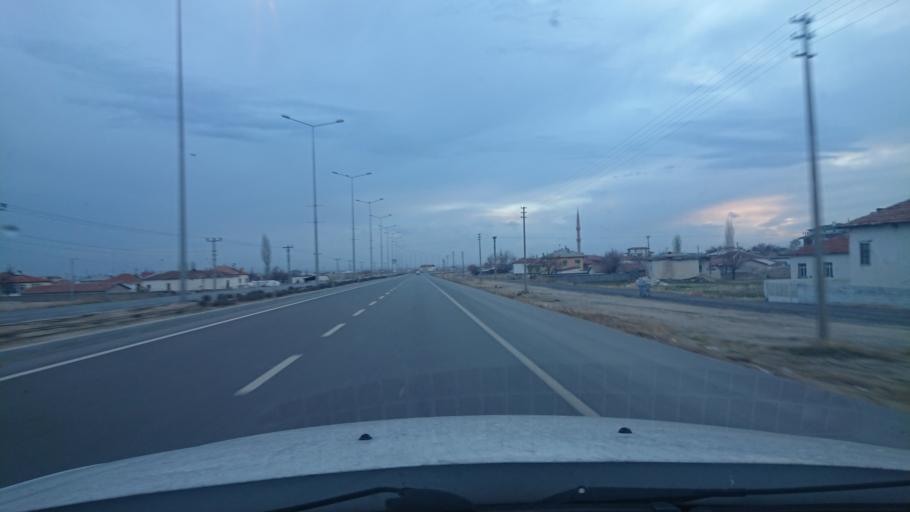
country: TR
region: Aksaray
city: Sultanhani
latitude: 38.2521
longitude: 33.5503
